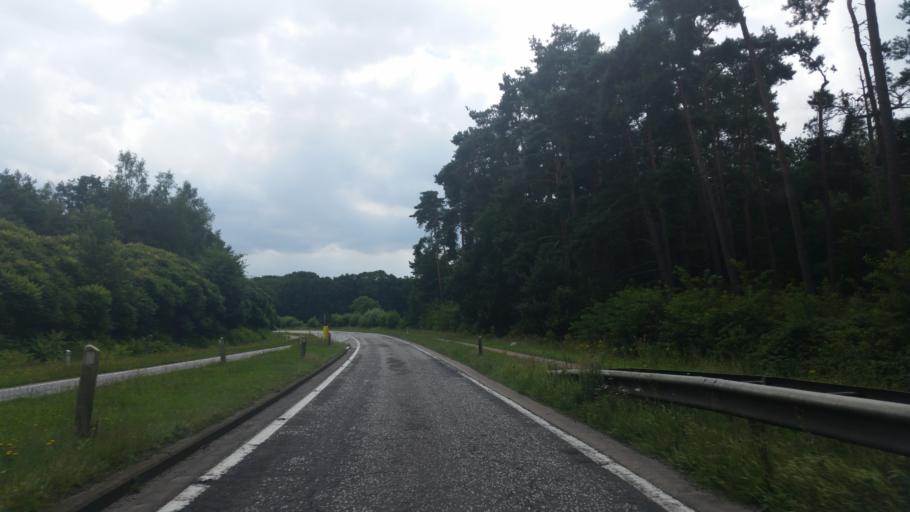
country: BE
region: Flanders
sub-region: Provincie Antwerpen
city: Vosselaar
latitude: 51.3238
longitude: 4.9139
